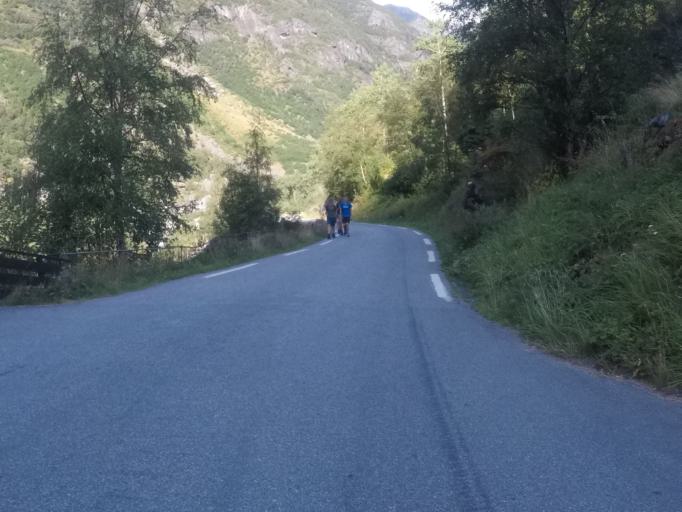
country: NO
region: Sogn og Fjordane
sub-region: Stryn
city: Stryn
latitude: 61.6639
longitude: 6.8228
